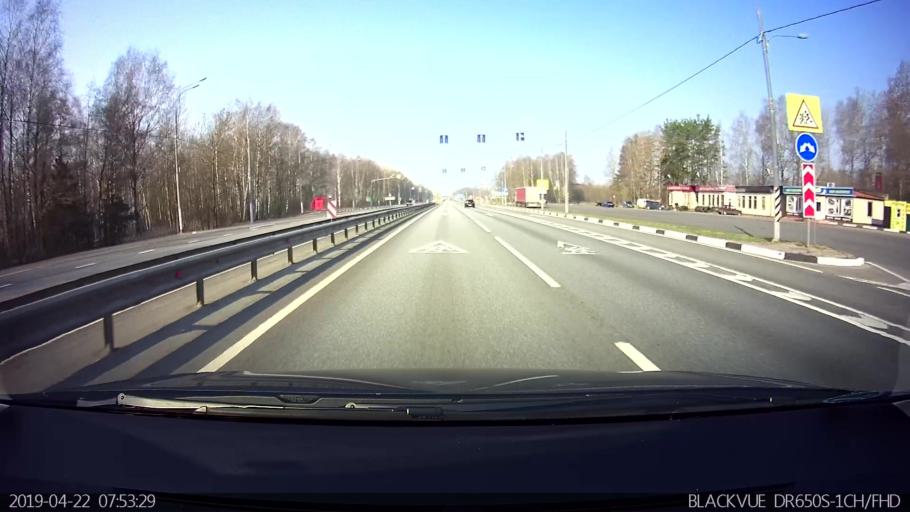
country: RU
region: Smolensk
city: Safonovo
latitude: 55.1439
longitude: 33.2749
